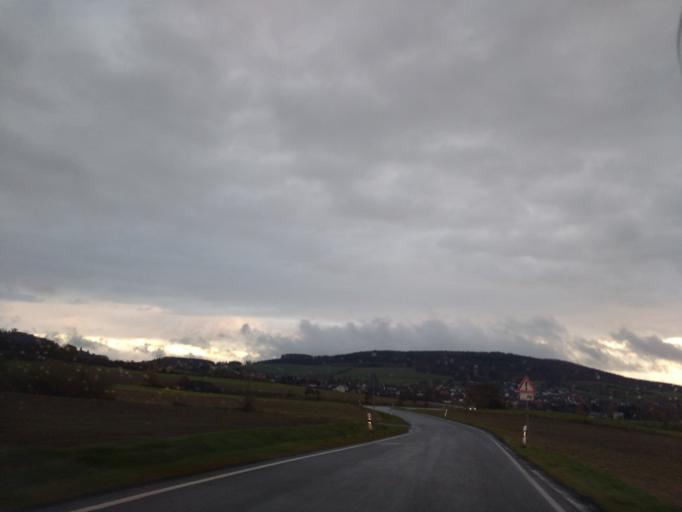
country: DE
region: Hesse
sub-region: Regierungsbezirk Kassel
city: Martinhagen
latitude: 51.2915
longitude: 9.3060
